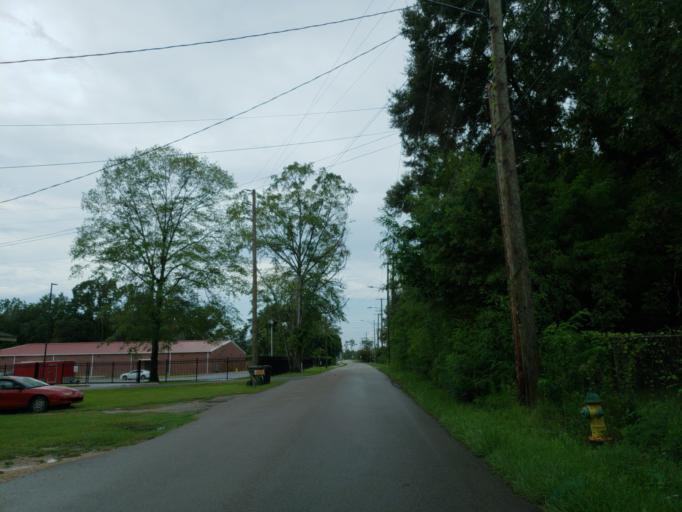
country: US
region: Mississippi
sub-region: Forrest County
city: Hattiesburg
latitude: 31.3030
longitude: -89.2871
